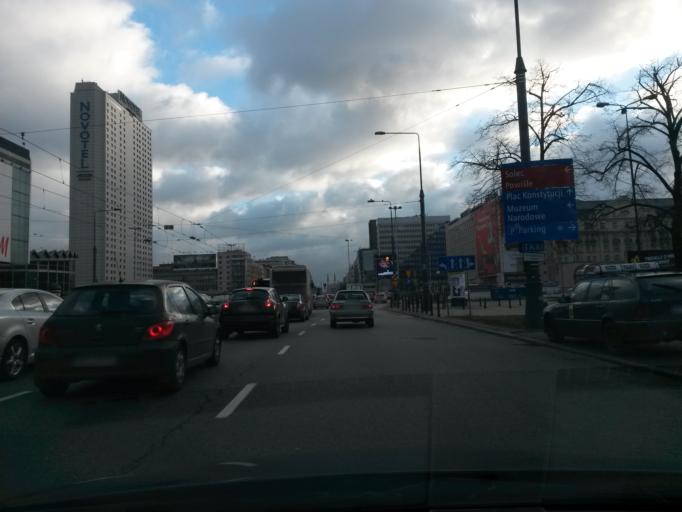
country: PL
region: Masovian Voivodeship
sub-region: Warszawa
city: Warsaw
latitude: 52.2313
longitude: 21.0107
